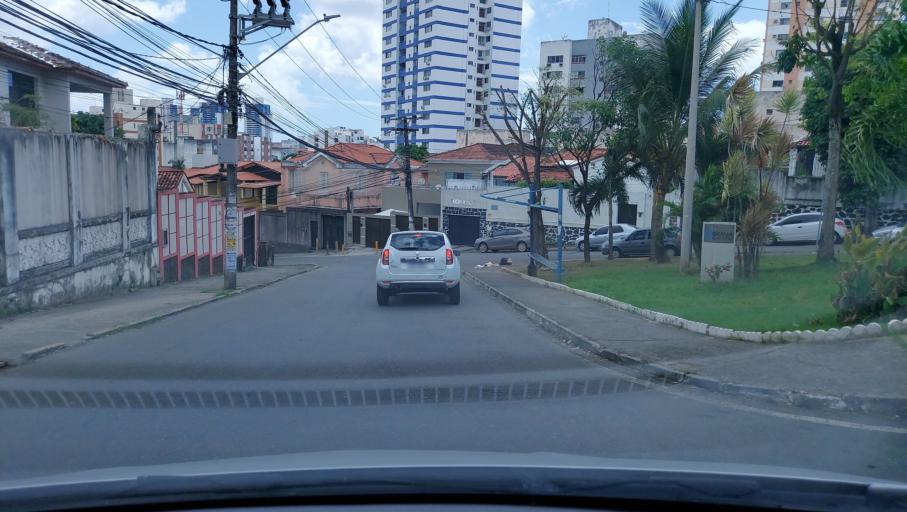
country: BR
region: Bahia
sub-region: Salvador
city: Salvador
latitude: -12.9735
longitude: -38.4918
